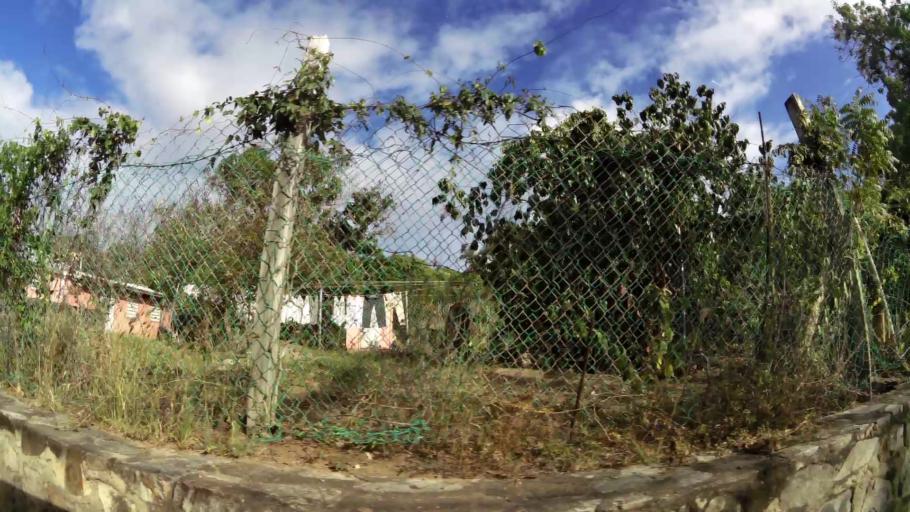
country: VG
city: Tortola
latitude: 18.4399
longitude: -64.4346
